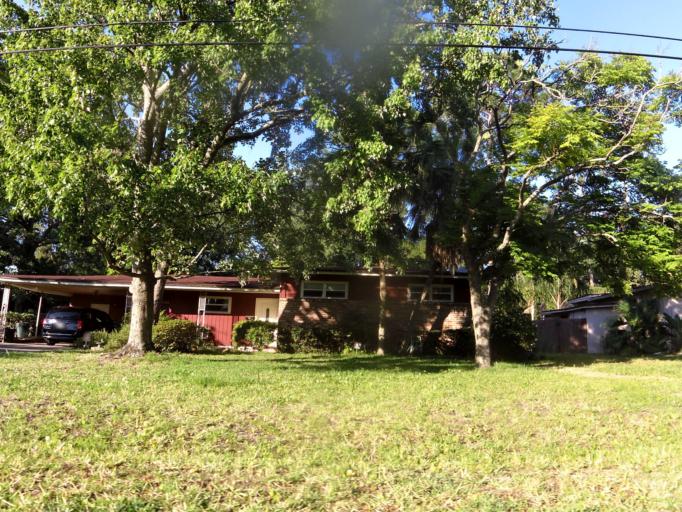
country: US
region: Florida
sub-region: Duval County
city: Jacksonville
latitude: 30.2374
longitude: -81.6168
